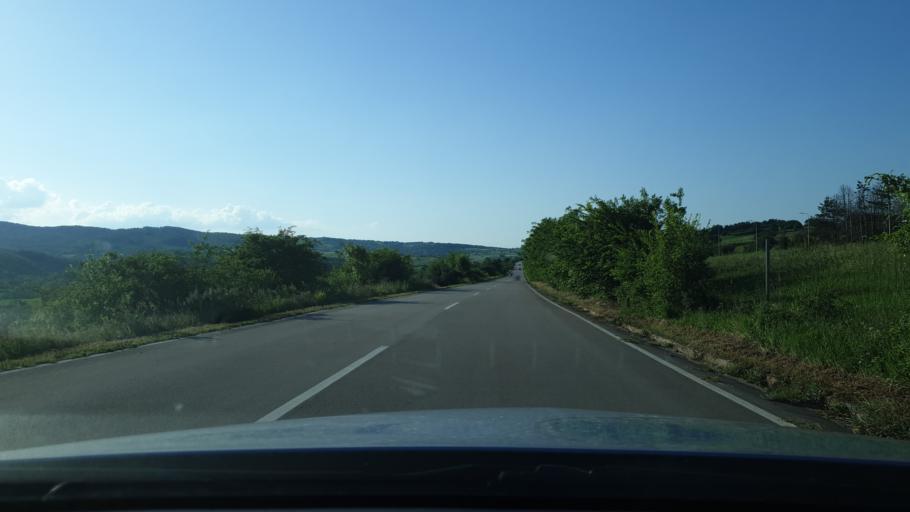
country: RS
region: Central Serbia
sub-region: Nisavski Okrug
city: Razanj
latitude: 43.6382
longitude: 21.5581
